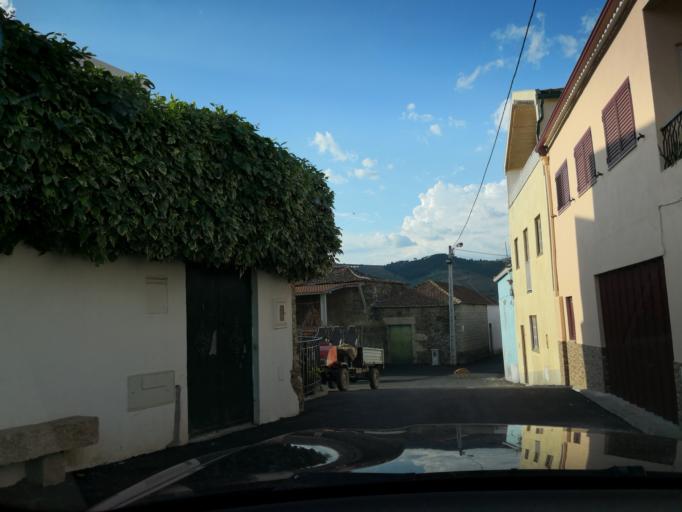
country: PT
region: Vila Real
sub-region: Santa Marta de Penaguiao
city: Santa Marta de Penaguiao
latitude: 41.2168
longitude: -7.7179
